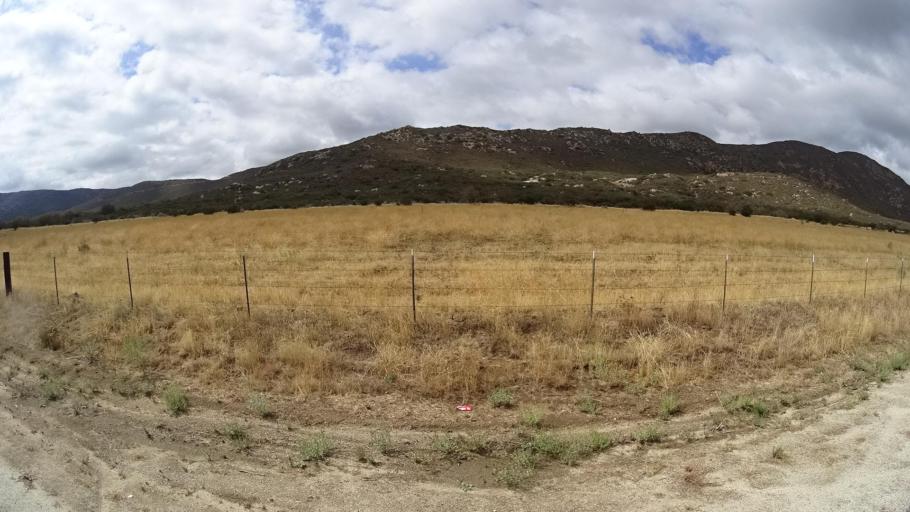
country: US
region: California
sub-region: San Diego County
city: Pine Valley
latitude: 32.7599
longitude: -116.4931
